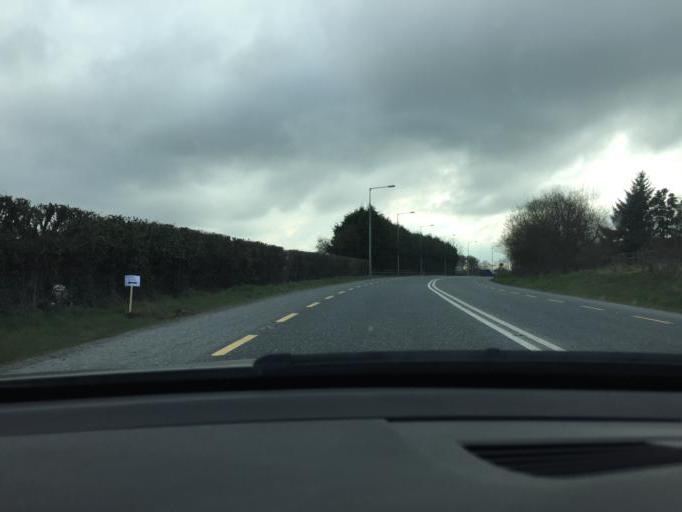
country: IE
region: Leinster
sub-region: South Dublin
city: Rathcoole
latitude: 53.2161
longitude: -6.4746
